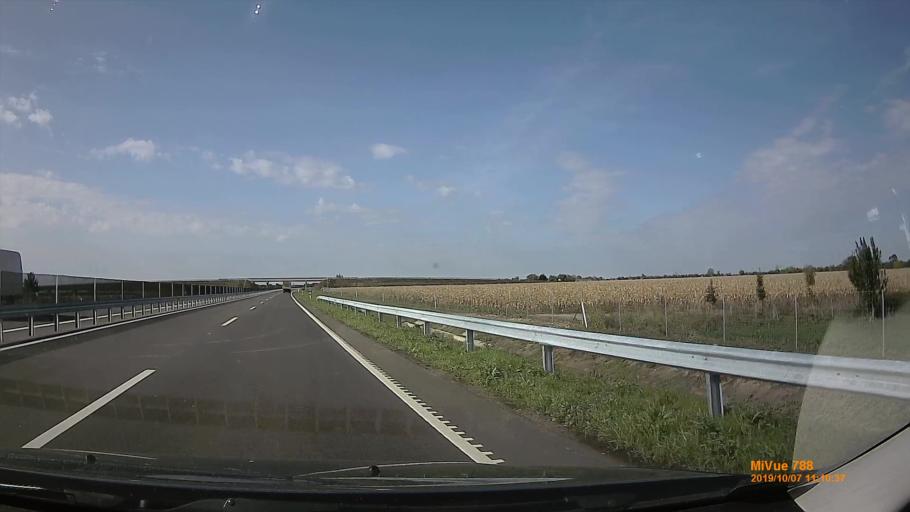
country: HU
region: Bekes
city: Kondoros
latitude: 46.7393
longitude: 20.8145
